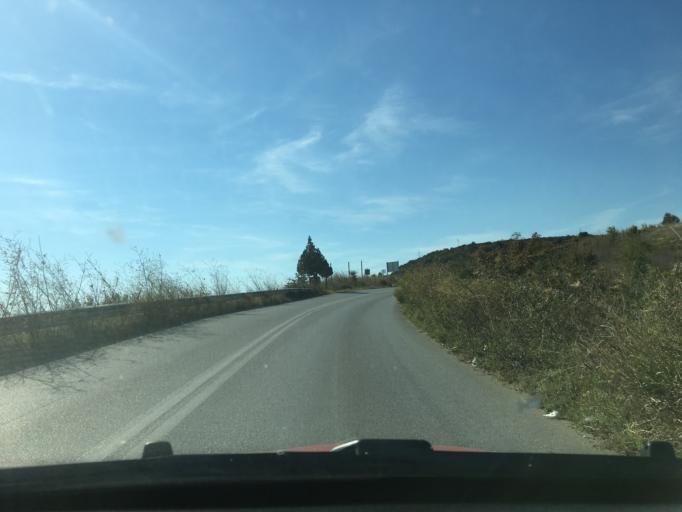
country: GR
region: Central Macedonia
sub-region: Nomos Chalkidikis
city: Nea Roda
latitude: 40.3801
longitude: 23.9170
